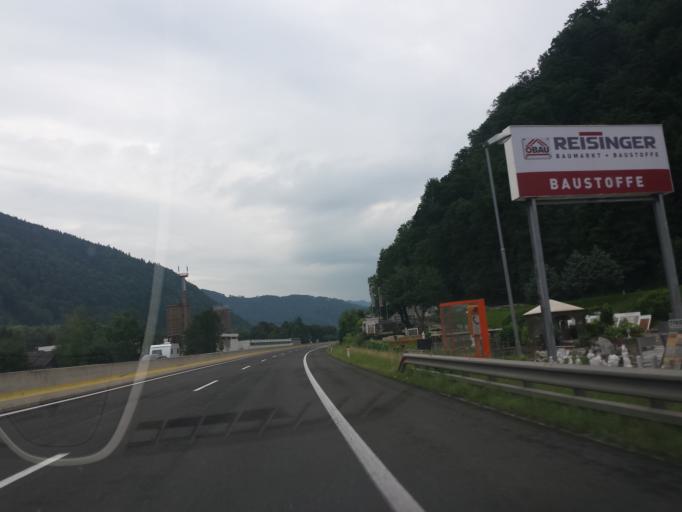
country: AT
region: Styria
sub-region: Politischer Bezirk Graz-Umgebung
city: Frohnleiten
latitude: 47.2470
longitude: 15.3168
